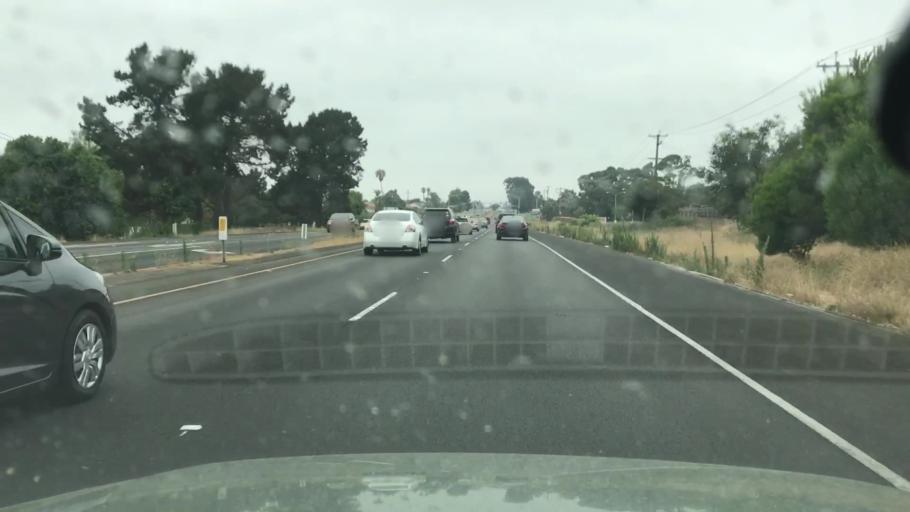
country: US
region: California
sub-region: Santa Barbara County
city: Orcutt
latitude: 34.9057
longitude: -120.4358
